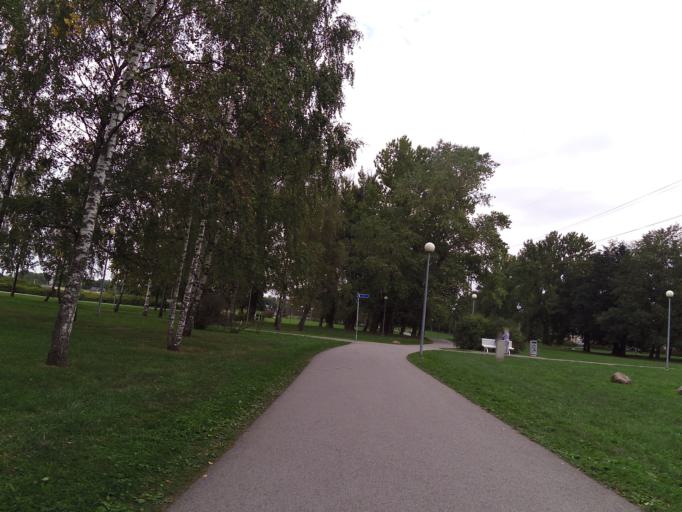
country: EE
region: Harju
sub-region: Tallinna linn
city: Tallinn
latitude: 59.4459
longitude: 24.6857
